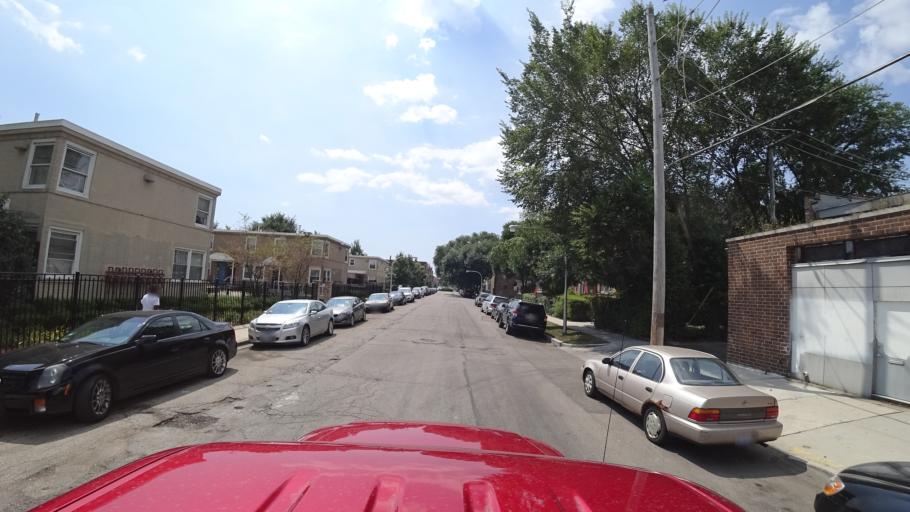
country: US
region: Illinois
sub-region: Cook County
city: Chicago
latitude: 41.8378
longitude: -87.6487
